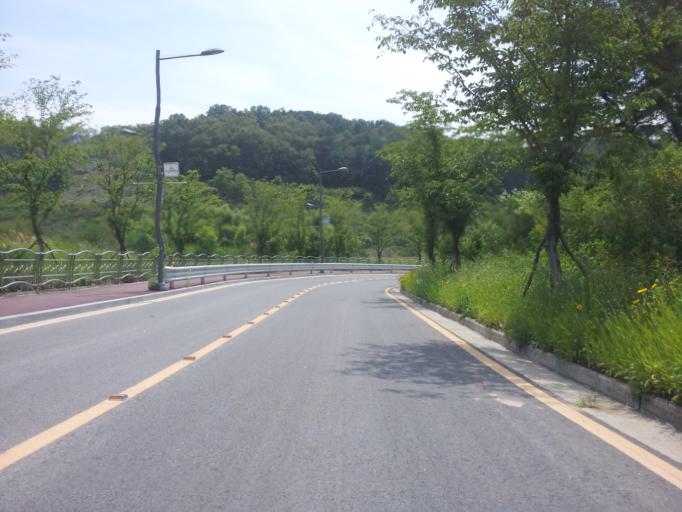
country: KR
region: Daejeon
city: Sintansin
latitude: 36.4564
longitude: 127.4730
